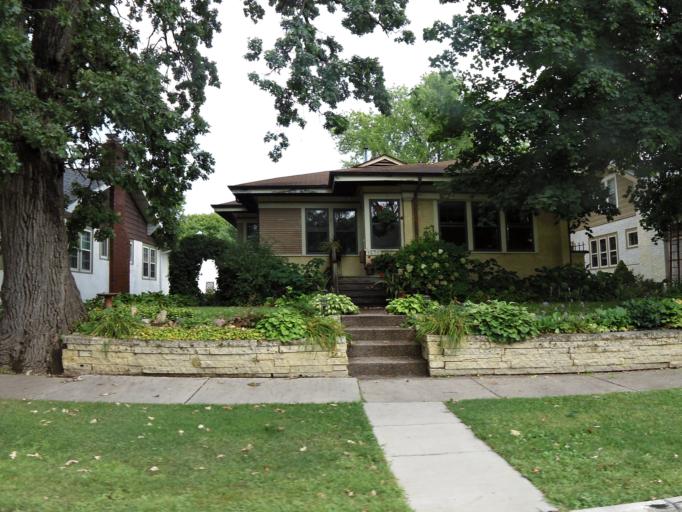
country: US
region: Minnesota
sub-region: Dakota County
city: Mendota Heights
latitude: 44.9307
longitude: -93.1709
